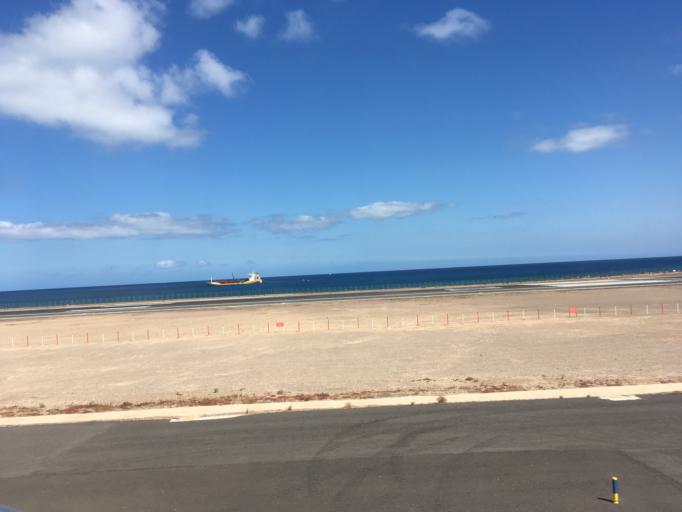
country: ES
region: Canary Islands
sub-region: Provincia de Las Palmas
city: Tias
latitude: 28.9381
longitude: -13.6116
